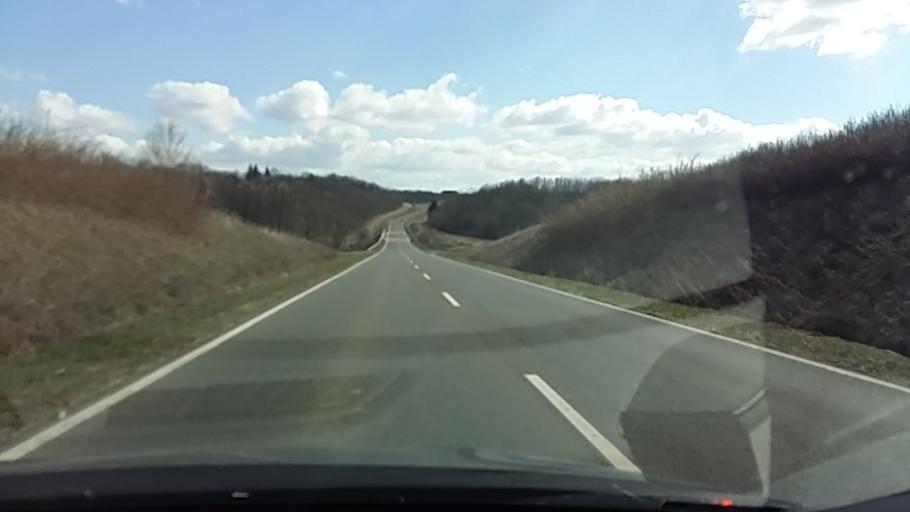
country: HU
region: Baranya
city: Kozarmisleny
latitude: 46.0290
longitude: 18.2766
